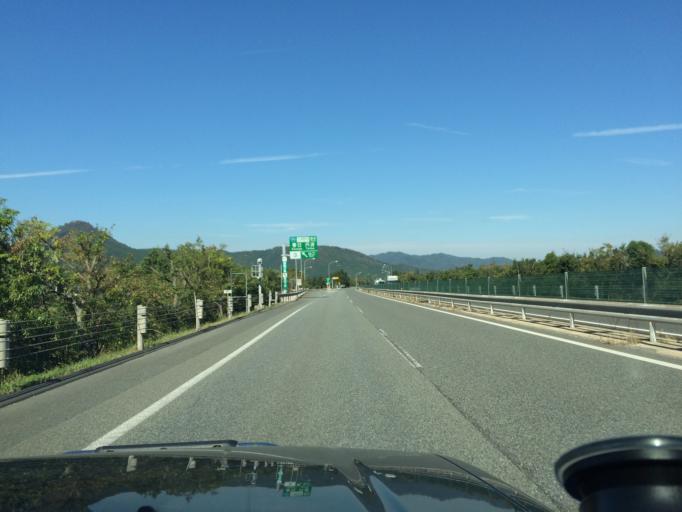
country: JP
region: Hyogo
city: Sasayama
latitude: 35.1608
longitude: 135.1196
